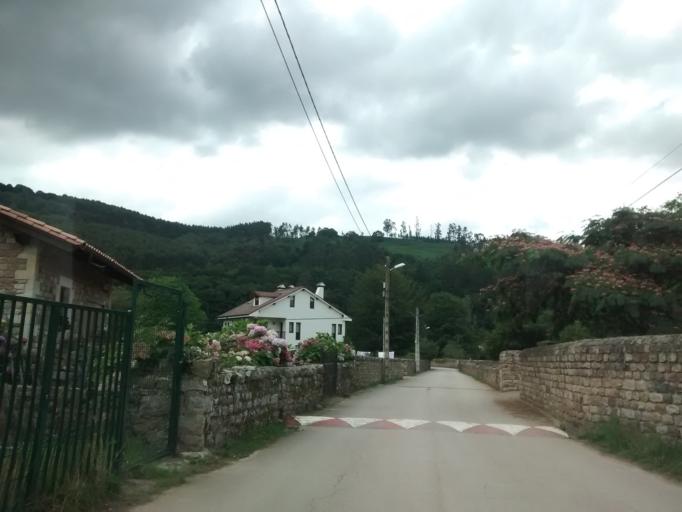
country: ES
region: Cantabria
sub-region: Provincia de Cantabria
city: Ruente
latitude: 43.2193
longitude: -4.2991
